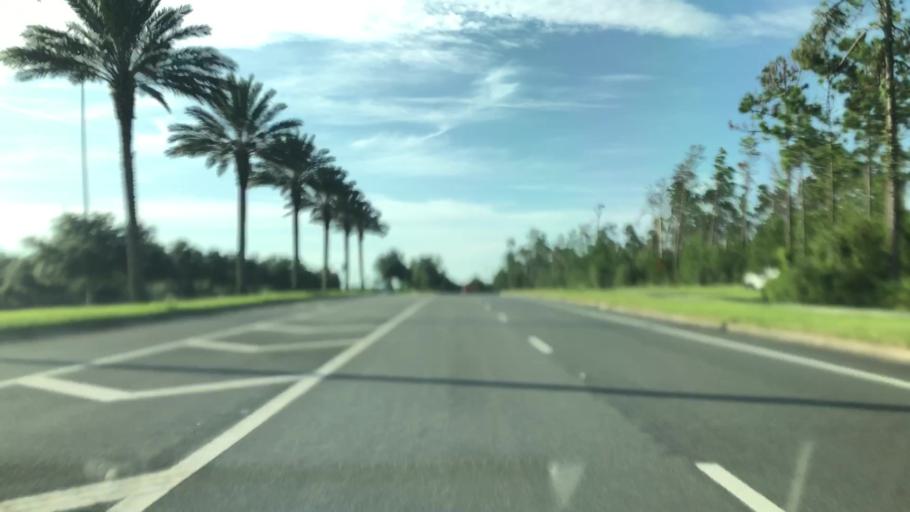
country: US
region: Florida
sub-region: Saint Johns County
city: Palm Valley
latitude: 30.1096
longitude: -81.4458
